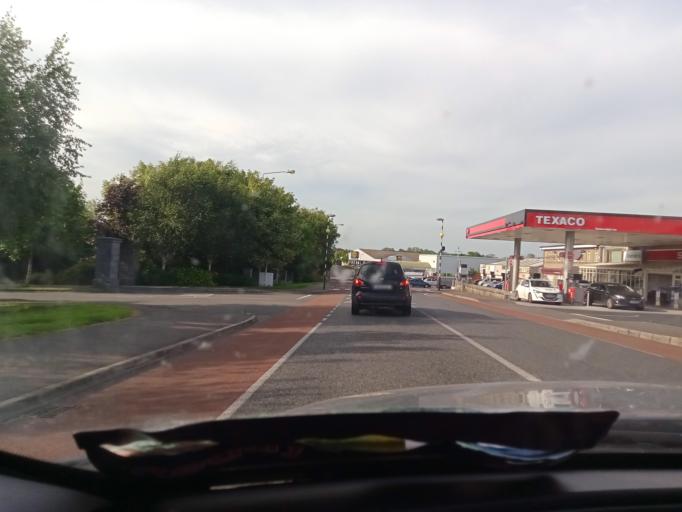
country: IE
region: Ulster
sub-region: An Cabhan
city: Cavan
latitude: 53.9746
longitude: -7.3546
